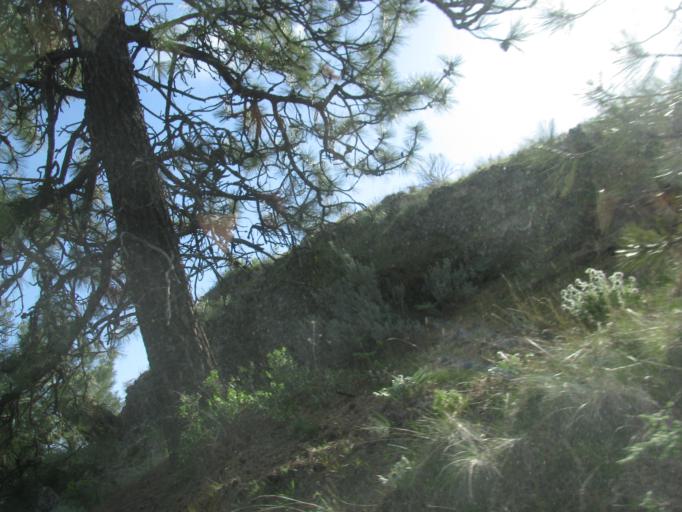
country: US
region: Washington
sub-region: Spokane County
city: Medical Lake
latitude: 47.3639
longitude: -117.8293
